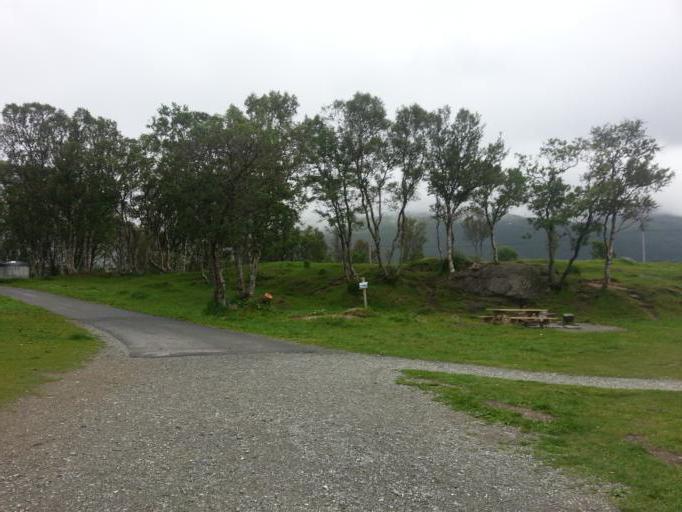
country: NO
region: Troms
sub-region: Tromso
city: Tromso
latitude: 69.6322
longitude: 18.9068
